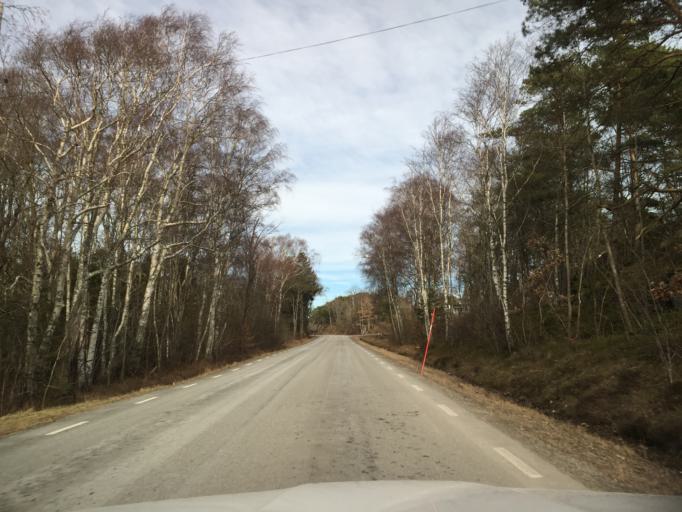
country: SE
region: Vaestra Goetaland
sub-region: Tjorns Kommun
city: Skaerhamn
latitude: 58.0266
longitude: 11.5377
